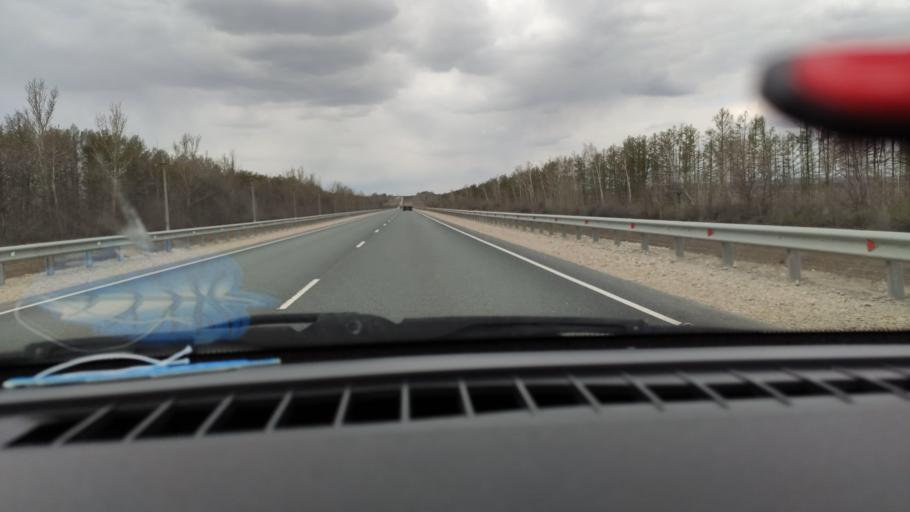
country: RU
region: Saratov
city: Shikhany
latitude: 52.1613
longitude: 47.1373
